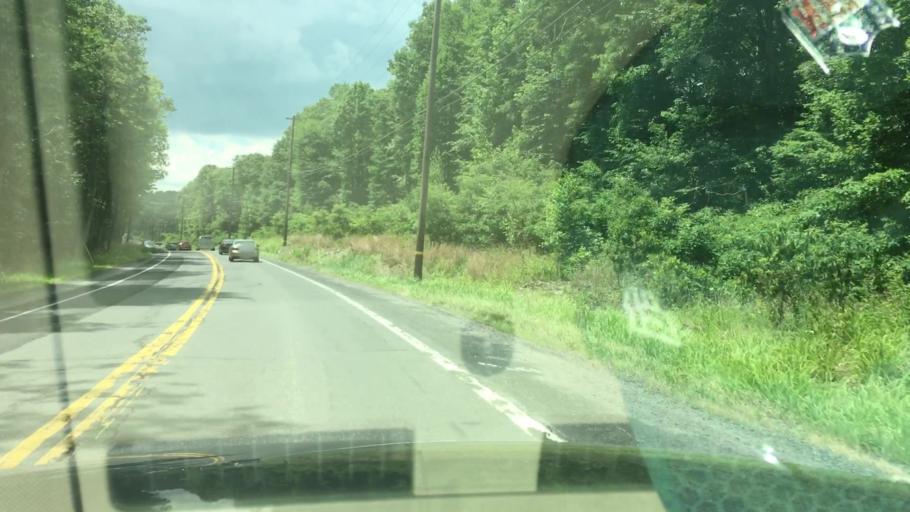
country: US
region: Pennsylvania
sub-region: Schuylkill County
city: Minersville
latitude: 40.7006
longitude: -76.3064
